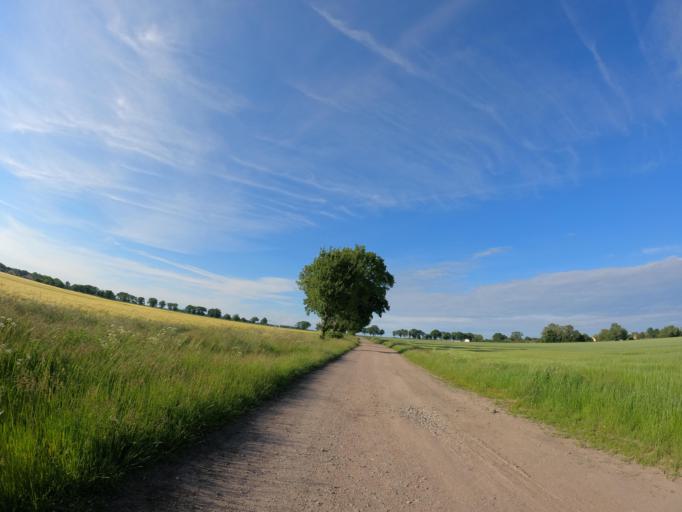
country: DE
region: Mecklenburg-Vorpommern
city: Preetz
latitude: 54.3439
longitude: 12.9992
